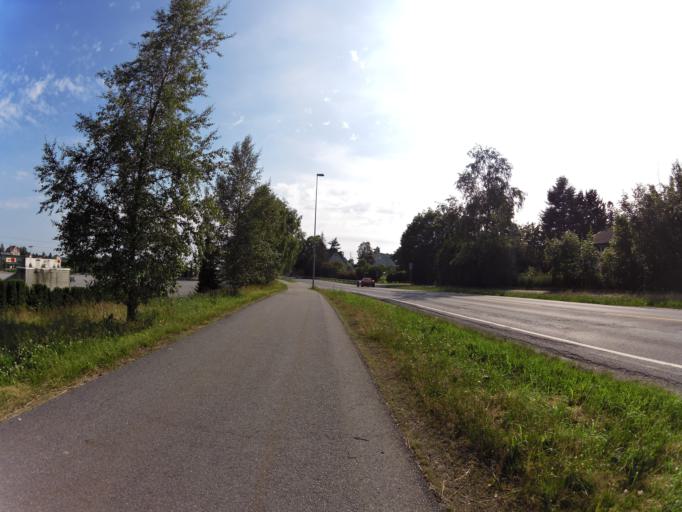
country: NO
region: Ostfold
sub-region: Fredrikstad
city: Fredrikstad
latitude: 59.2513
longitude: 10.9910
